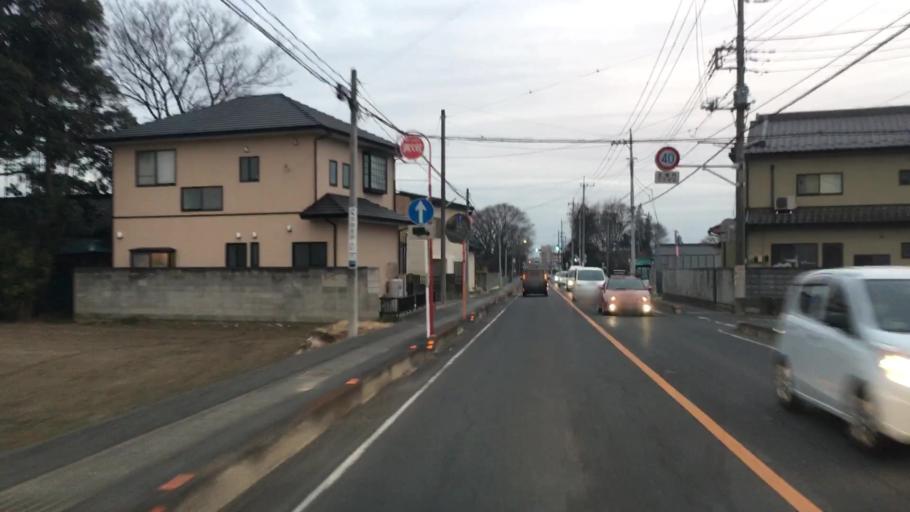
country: JP
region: Gunma
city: Ota
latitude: 36.3087
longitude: 139.3601
